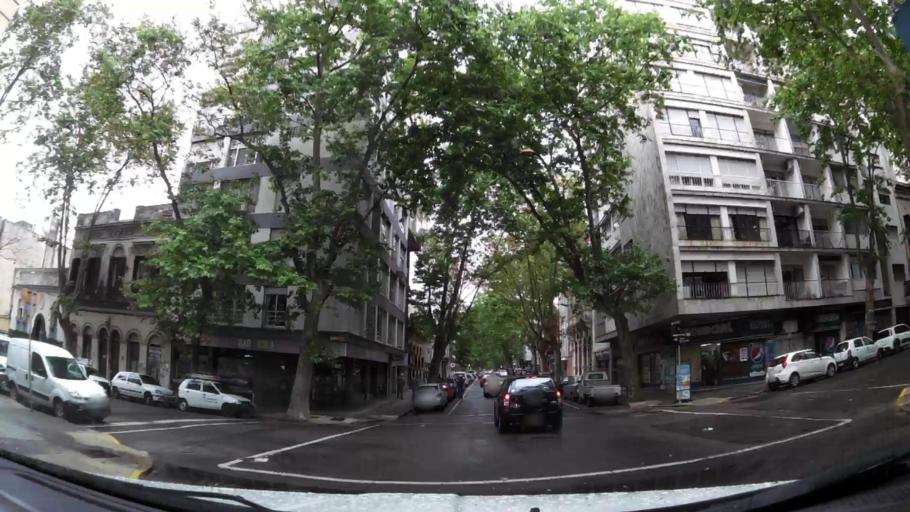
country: UY
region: Montevideo
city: Montevideo
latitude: -34.9087
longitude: -56.1910
